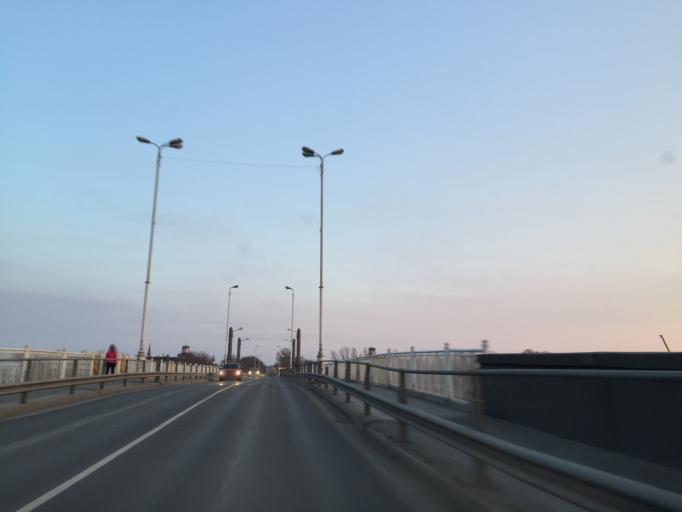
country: EE
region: Paernumaa
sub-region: Paernu linn
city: Parnu
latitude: 58.3902
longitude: 24.4955
